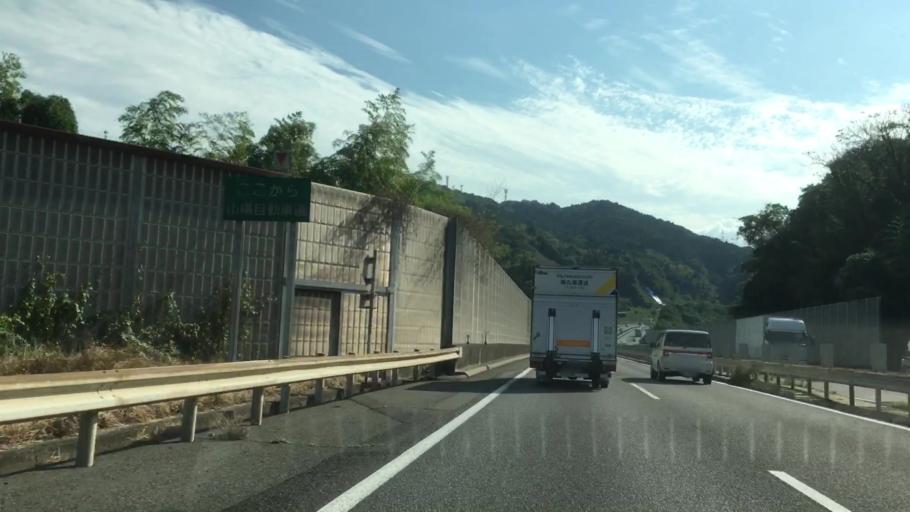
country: JP
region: Yamaguchi
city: Otake
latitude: 34.2376
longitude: 132.2143
